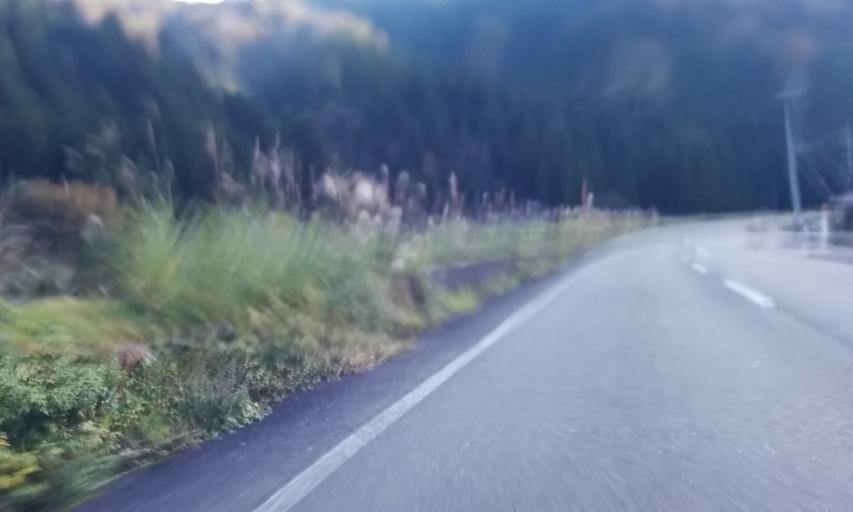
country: JP
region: Fukui
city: Obama
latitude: 35.3982
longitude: 135.6101
